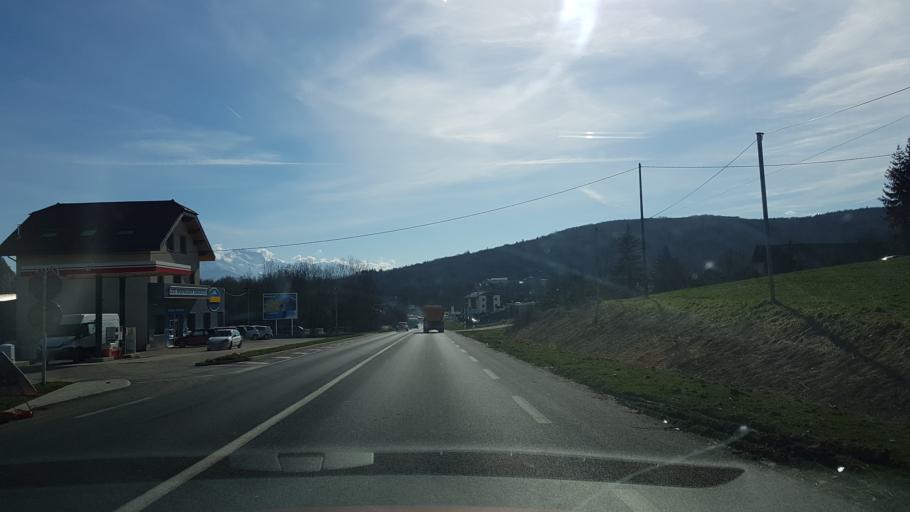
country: FR
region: Rhone-Alpes
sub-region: Departement de la Haute-Savoie
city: Sillingy
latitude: 45.9492
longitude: 6.0455
